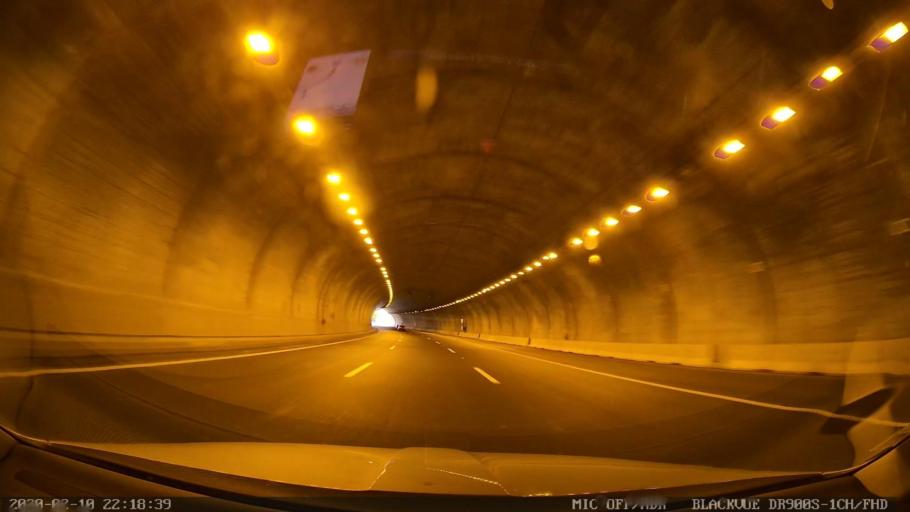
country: PT
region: Lisbon
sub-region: Arruda Dos Vinhos
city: Arruda dos Vinhos
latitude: 38.9415
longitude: -9.0678
